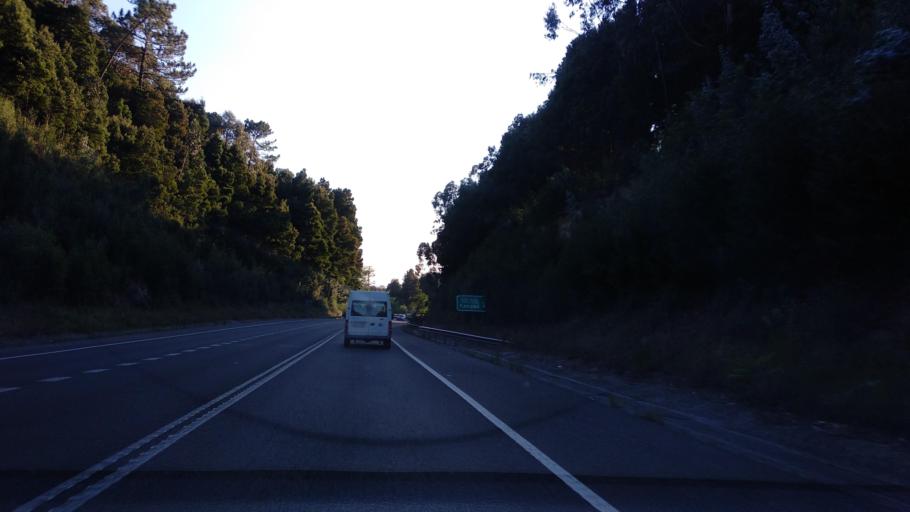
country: ES
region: Galicia
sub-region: Provincia de Pontevedra
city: Moana
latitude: 42.2740
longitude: -8.7577
